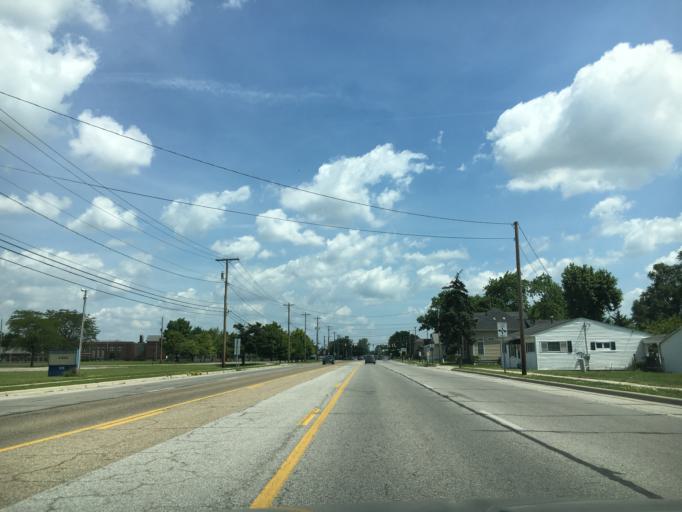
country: US
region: Ohio
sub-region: Franklin County
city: Lincoln Village
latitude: 39.9473
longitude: -83.1408
